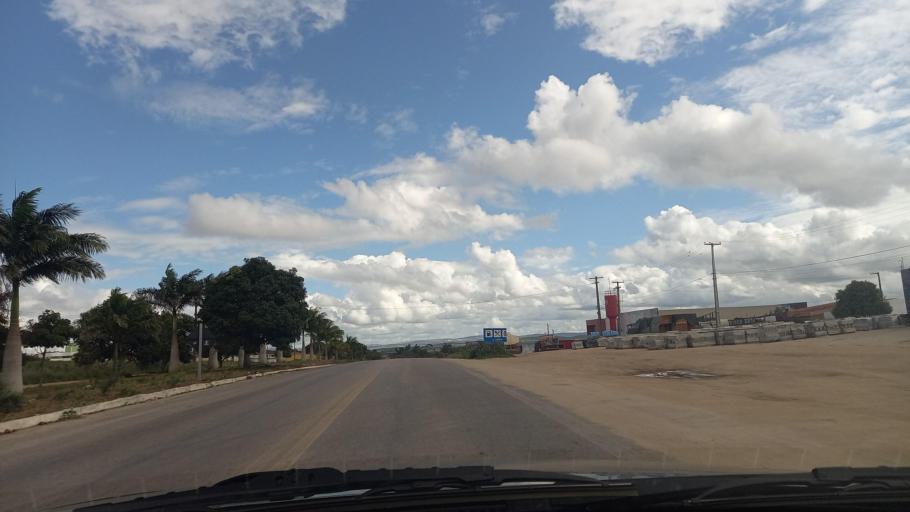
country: BR
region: Pernambuco
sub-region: Lajedo
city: Lajedo
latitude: -8.7146
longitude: -36.4214
